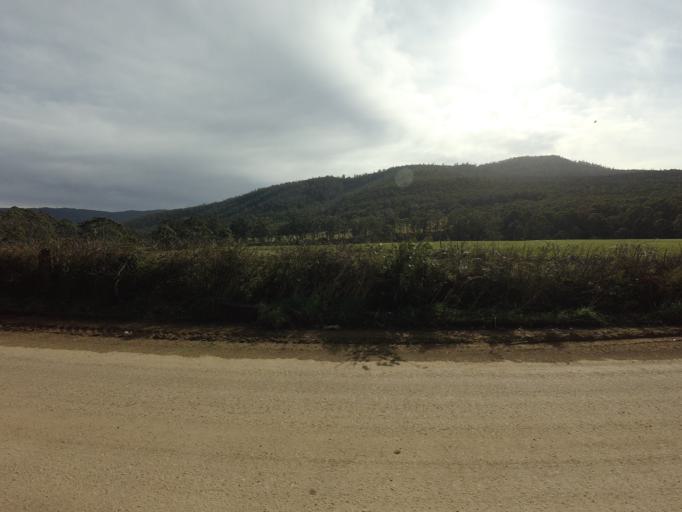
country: AU
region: Tasmania
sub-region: Huon Valley
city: Huonville
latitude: -43.0760
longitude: 147.0630
